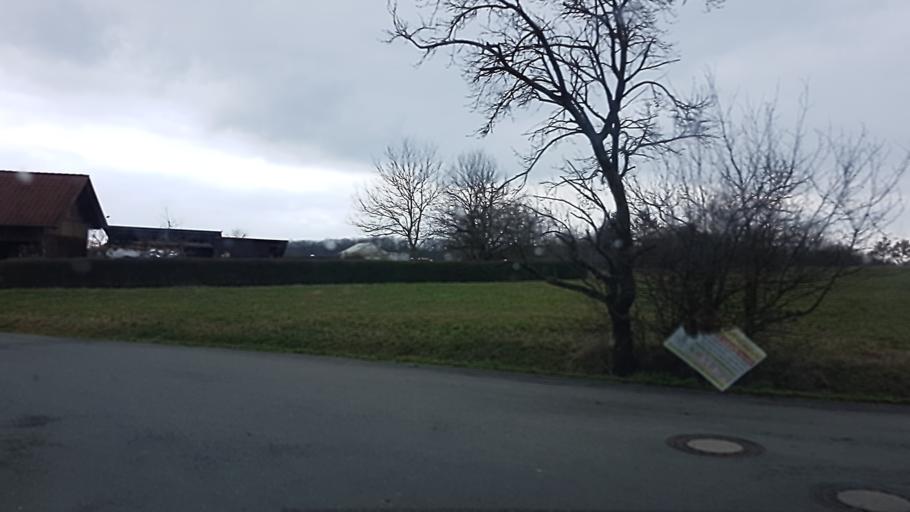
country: DE
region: Bavaria
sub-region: Upper Franconia
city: Litzendorf
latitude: 49.9315
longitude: 11.0086
